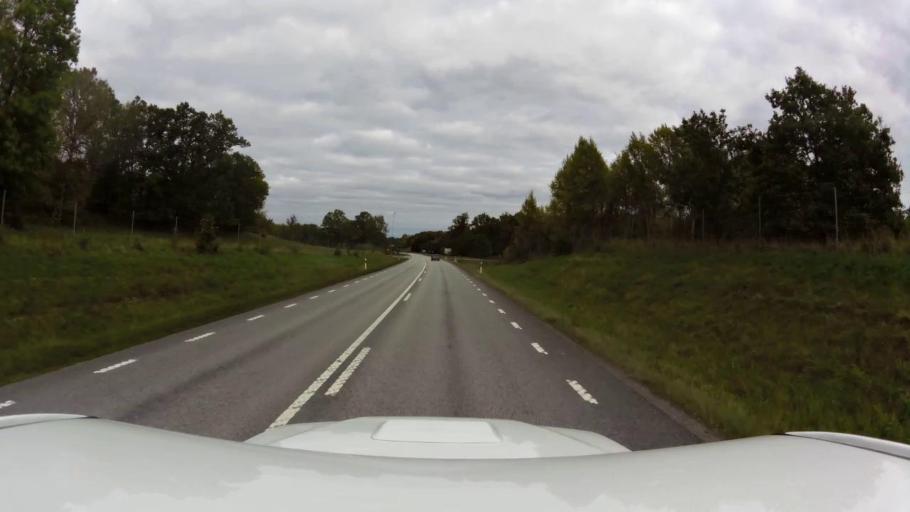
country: SE
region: OEstergoetland
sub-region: Kinda Kommun
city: Rimforsa
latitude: 58.2089
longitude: 15.6688
